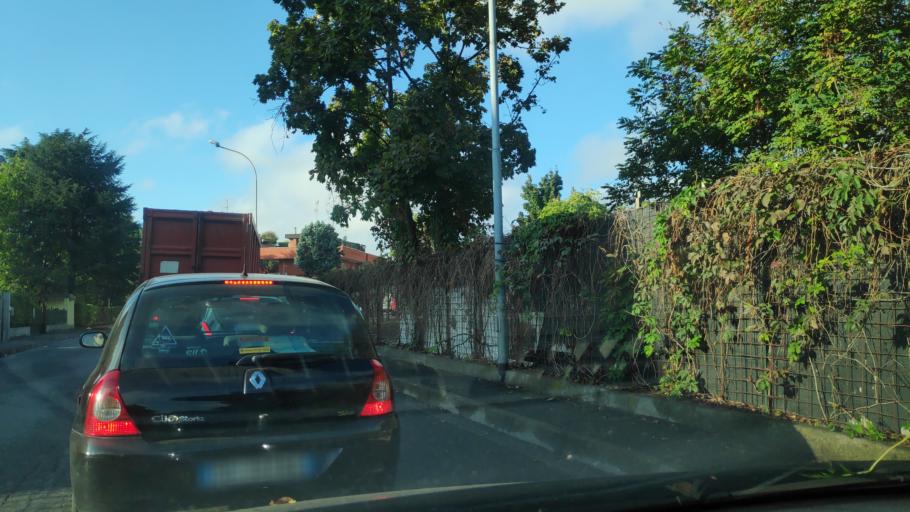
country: IT
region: Lombardy
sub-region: Citta metropolitana di Milano
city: Fizzonasco
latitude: 45.3743
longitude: 9.1881
